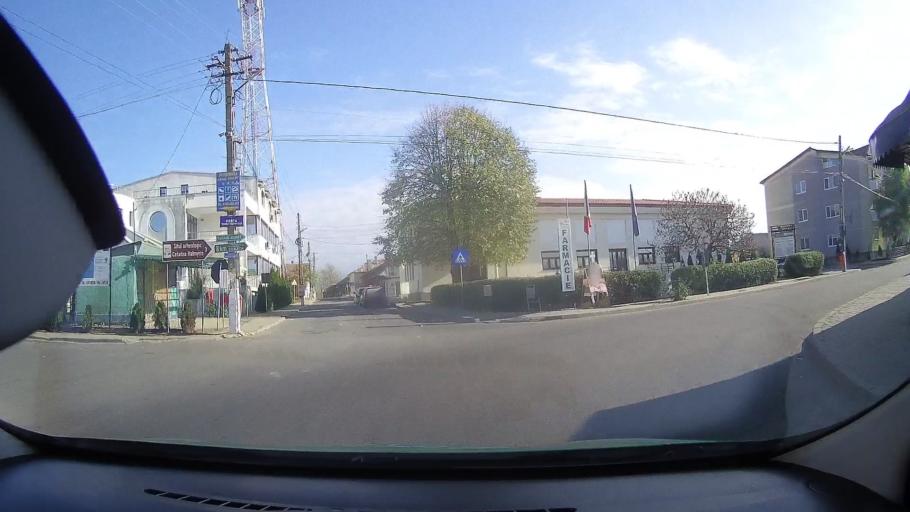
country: RO
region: Tulcea
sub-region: Comuna Murighiol
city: Murighiol
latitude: 45.0377
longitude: 29.1645
